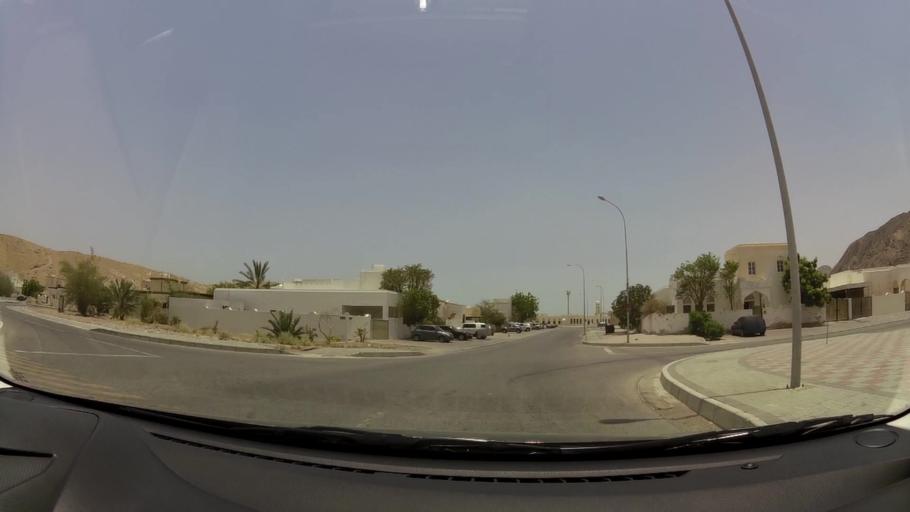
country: OM
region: Muhafazat Masqat
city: Bawshar
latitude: 23.5645
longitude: 58.4232
